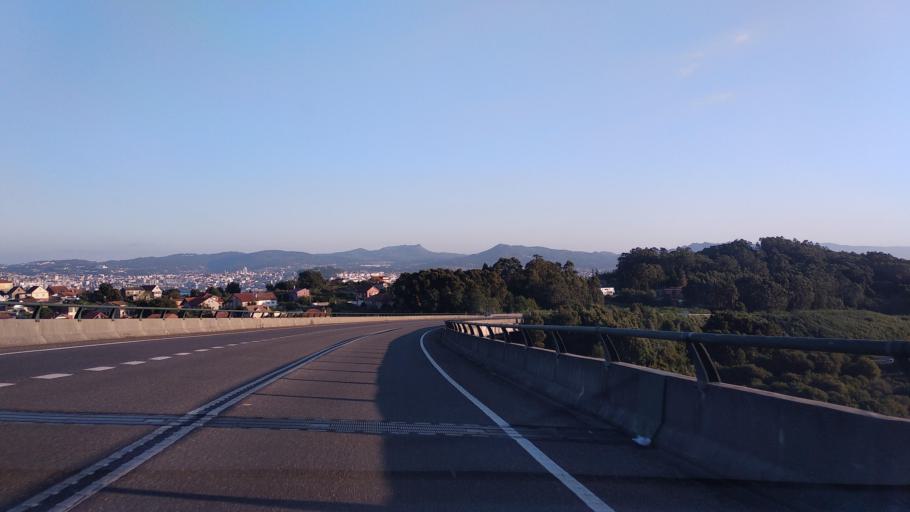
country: ES
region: Galicia
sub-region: Provincia de Pontevedra
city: Moana
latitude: 42.2822
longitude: -8.7526
